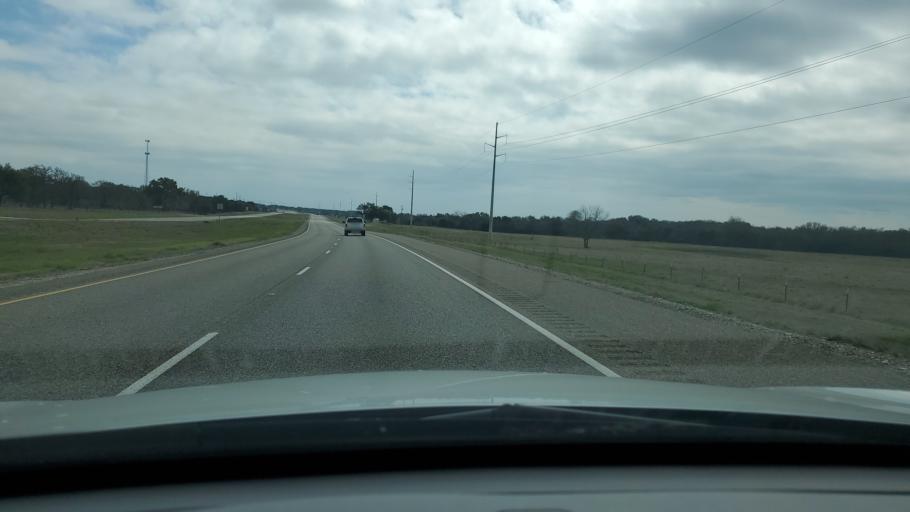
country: US
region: Texas
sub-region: Williamson County
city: Florence
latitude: 30.7697
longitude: -97.7560
